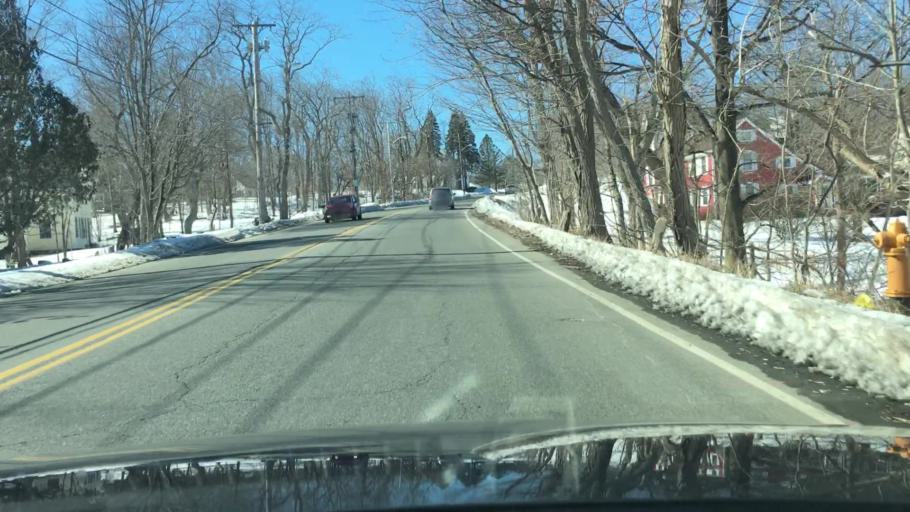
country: US
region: Massachusetts
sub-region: Essex County
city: Amesbury
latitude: 42.8489
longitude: -70.9091
